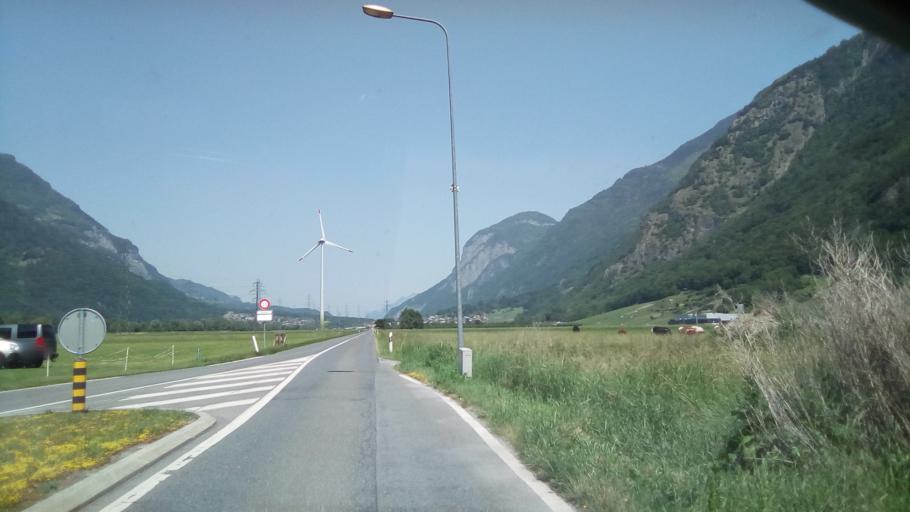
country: CH
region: Valais
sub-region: Saint-Maurice District
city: Vernayaz
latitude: 46.1531
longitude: 7.0412
